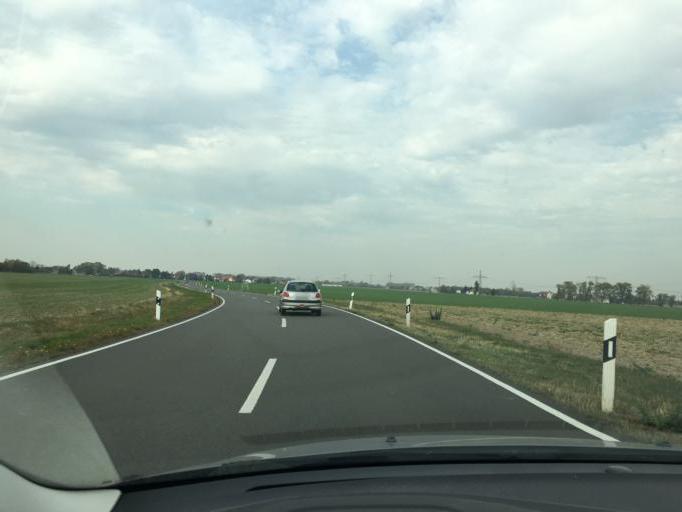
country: DE
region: Saxony
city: Zwochau
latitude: 51.4495
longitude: 12.2690
